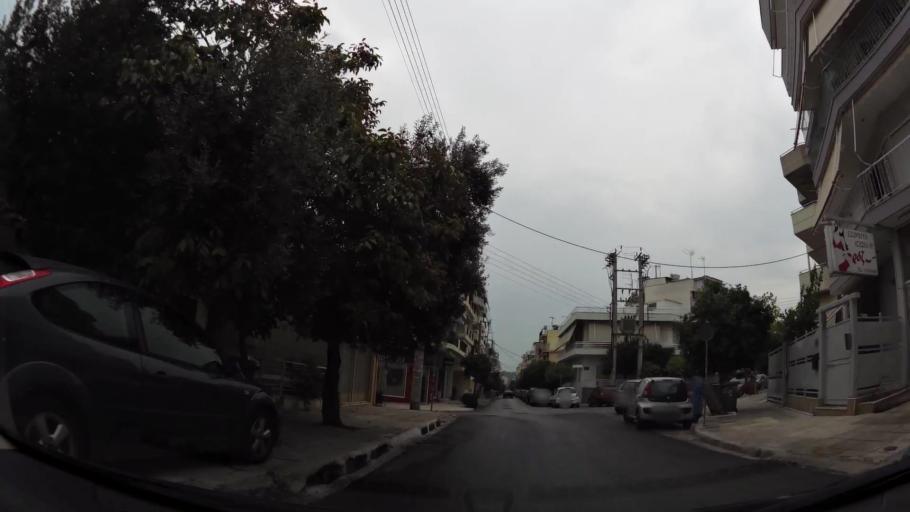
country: GR
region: Attica
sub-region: Nomos Piraios
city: Korydallos
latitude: 37.9843
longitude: 23.6444
